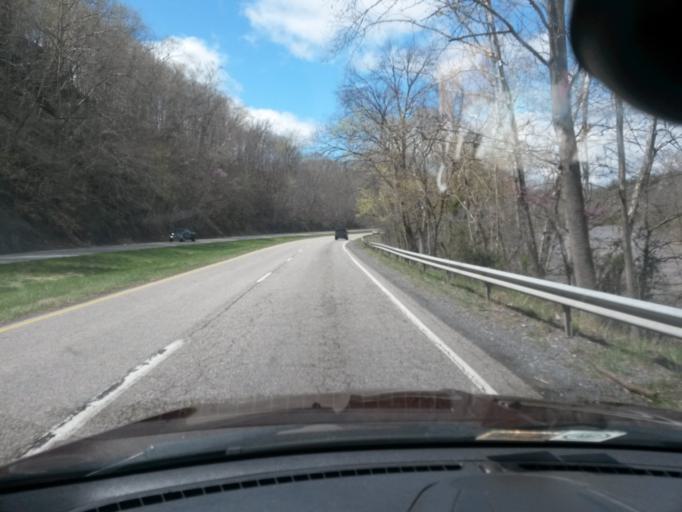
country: US
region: Virginia
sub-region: City of Buena Vista
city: Buena Vista
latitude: 37.7496
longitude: -79.3896
